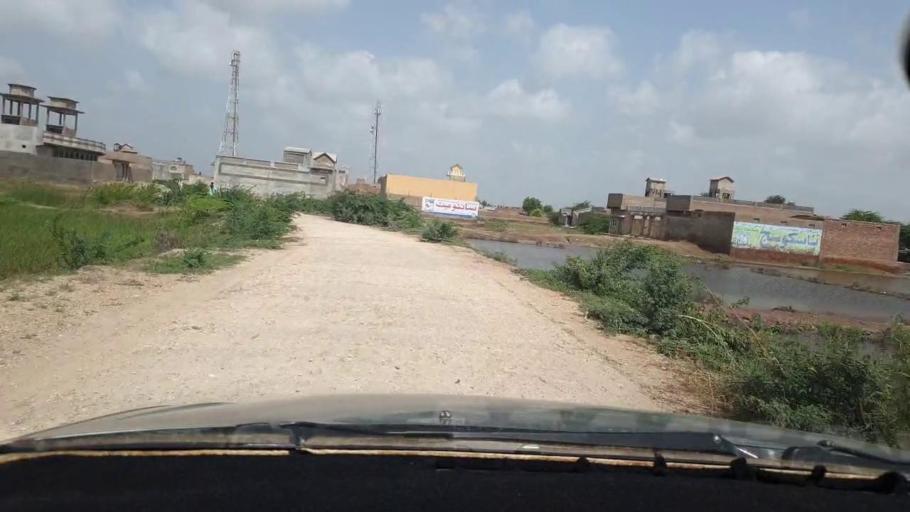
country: PK
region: Sindh
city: Tando Bago
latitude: 24.7601
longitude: 69.1916
